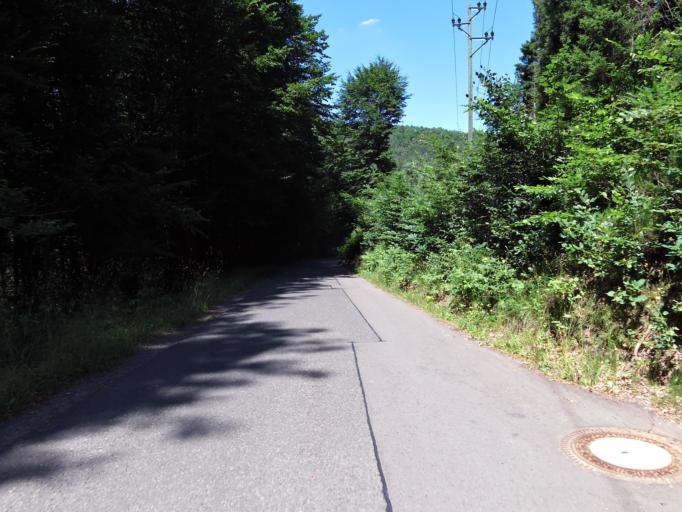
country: DE
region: Rheinland-Pfalz
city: Frankeneck
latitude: 49.3627
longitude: 8.0302
